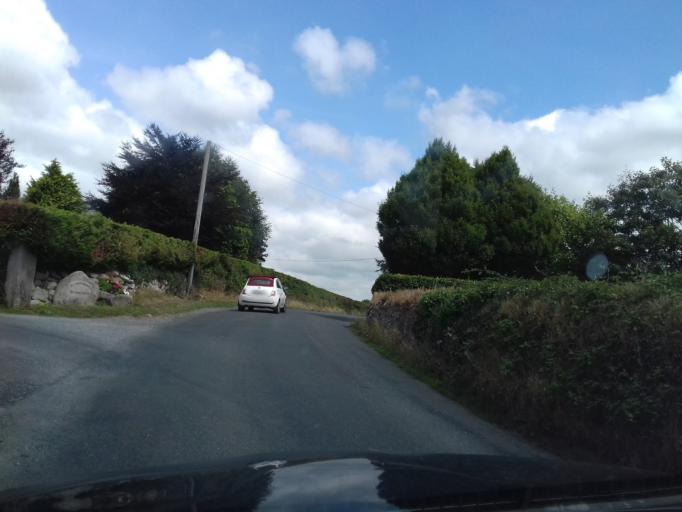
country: IE
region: Leinster
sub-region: Kilkenny
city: Graiguenamanagh
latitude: 52.5991
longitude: -6.9152
